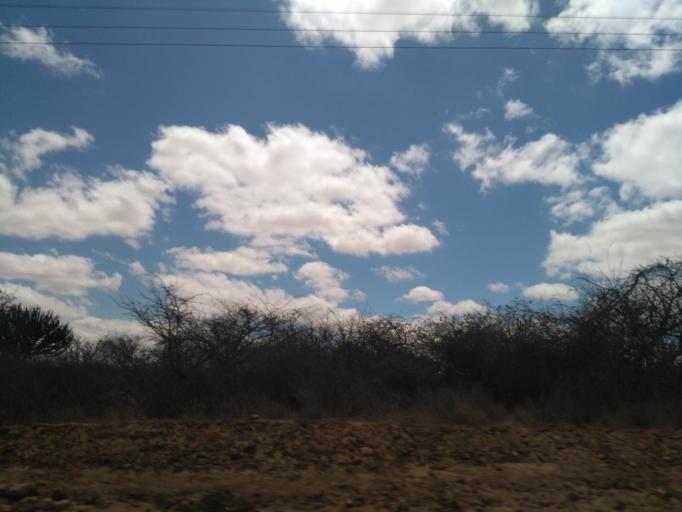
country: TZ
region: Dodoma
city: Dodoma
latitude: -6.2088
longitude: 35.7567
